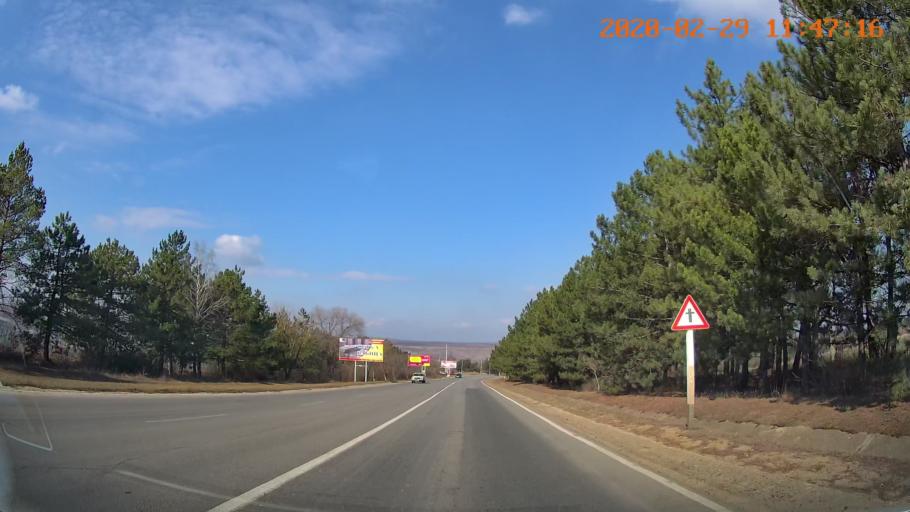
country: MD
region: Rezina
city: Rezina
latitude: 47.7390
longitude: 28.9891
